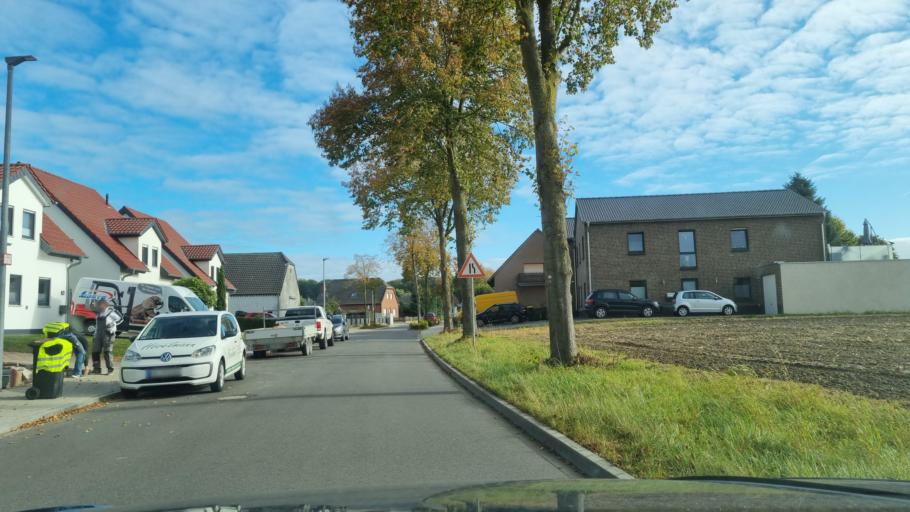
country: DE
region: North Rhine-Westphalia
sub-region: Regierungsbezirk Dusseldorf
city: Kranenburg
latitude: 51.7861
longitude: 6.0575
